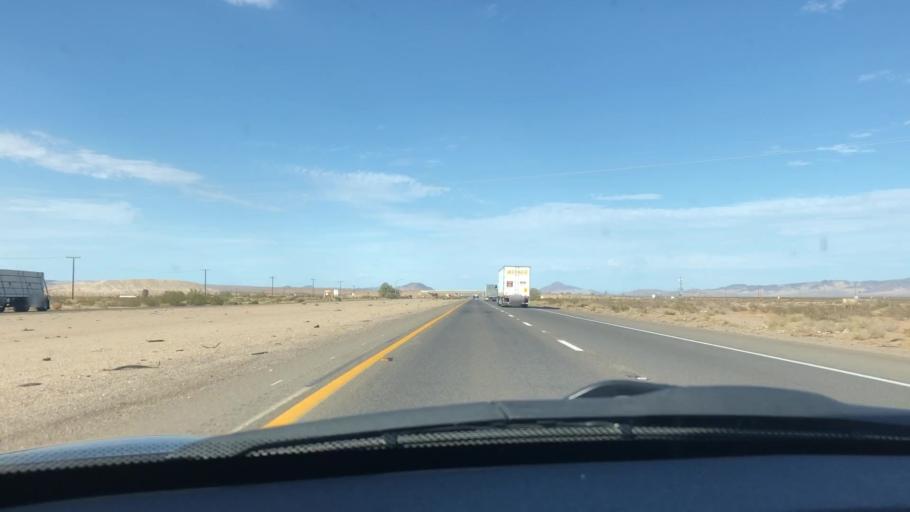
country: US
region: California
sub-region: San Bernardino County
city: Fort Irwin
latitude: 34.9596
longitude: -116.6537
